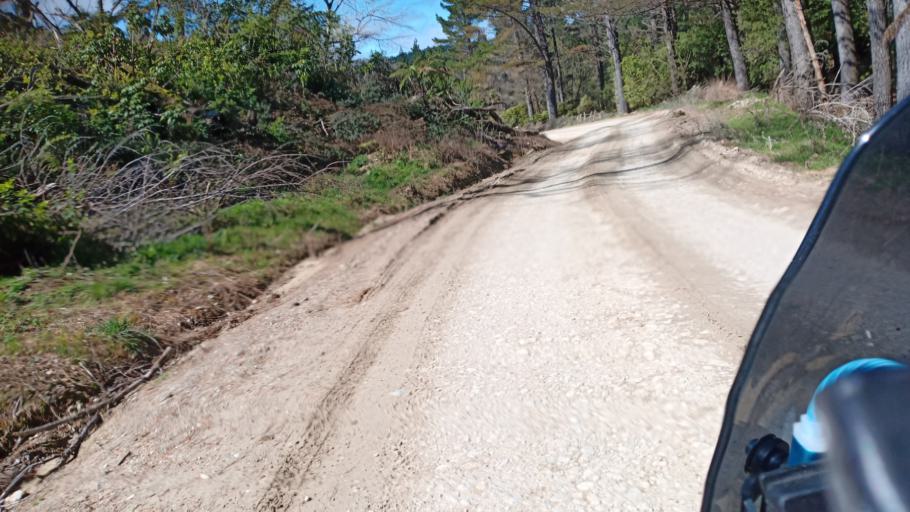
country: NZ
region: Gisborne
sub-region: Gisborne District
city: Gisborne
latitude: -38.8920
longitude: 177.7932
